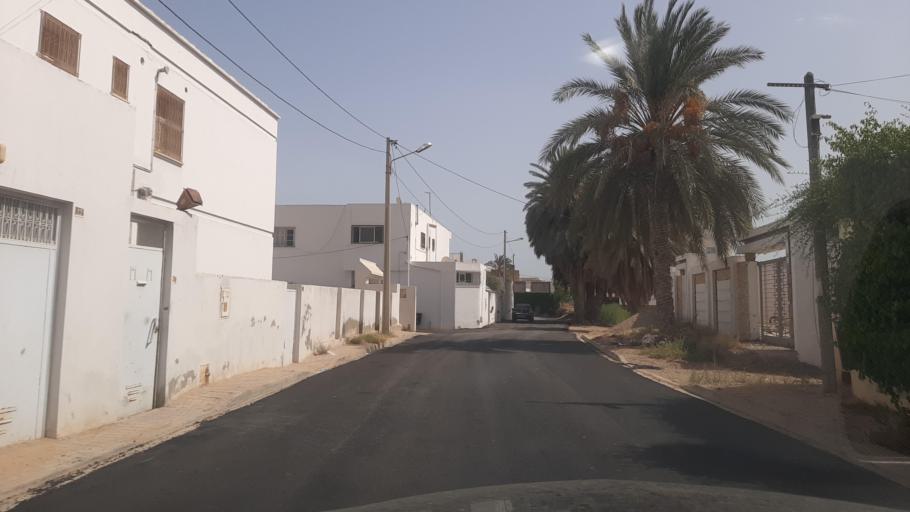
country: TN
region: Safaqis
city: Sfax
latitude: 34.7588
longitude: 10.7583
